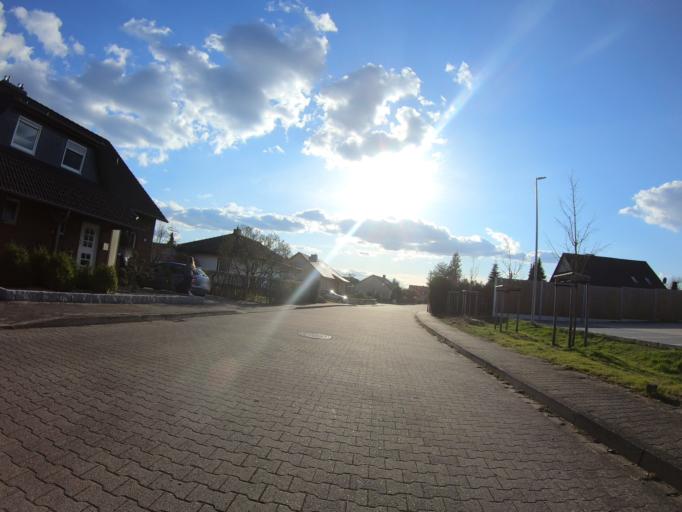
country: DE
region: Lower Saxony
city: Wesendorf
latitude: 52.5926
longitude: 10.5407
